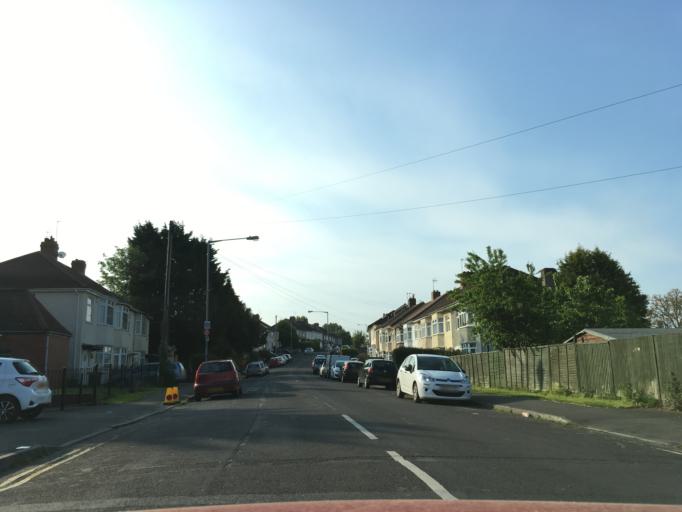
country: GB
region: England
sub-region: Bristol
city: Bristol
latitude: 51.4971
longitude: -2.5972
